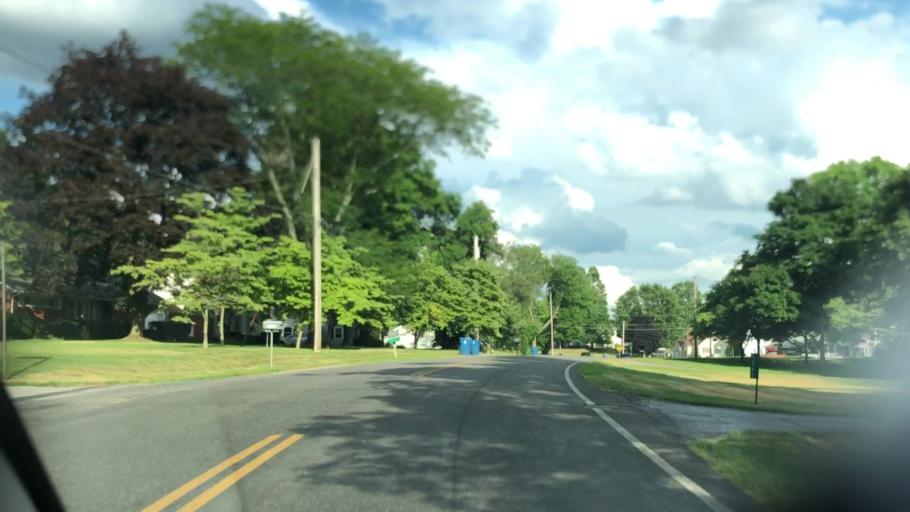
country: US
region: Ohio
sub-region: Summit County
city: Norton
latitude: 41.0217
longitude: -81.6279
